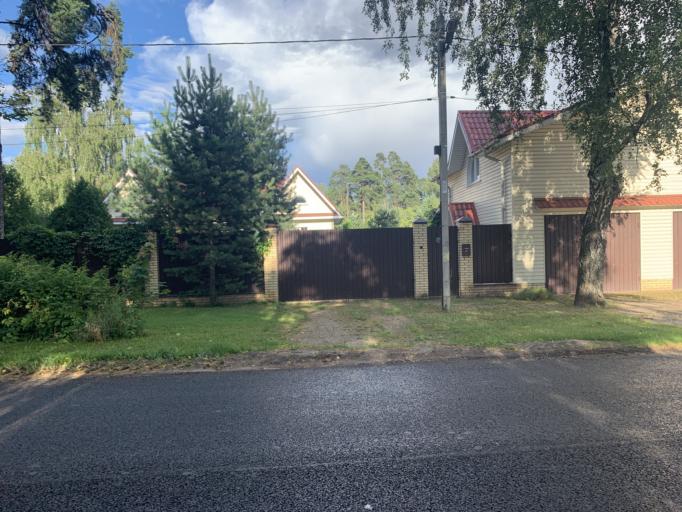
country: RU
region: Moskovskaya
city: Mamontovka
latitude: 55.9737
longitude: 37.8432
